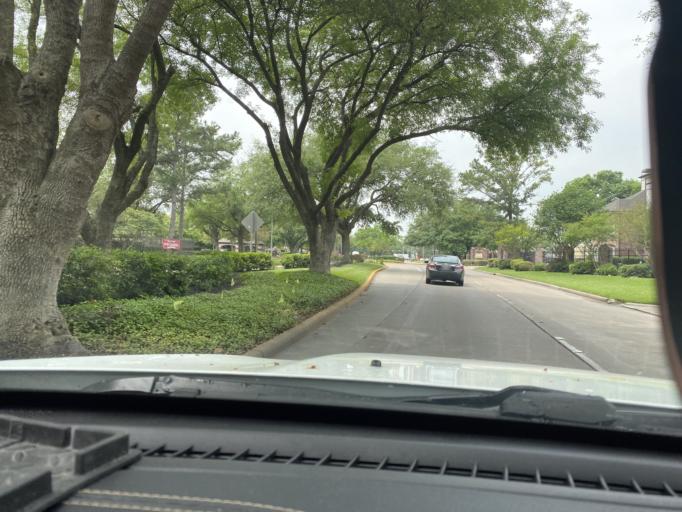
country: US
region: Texas
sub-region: Harris County
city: Jersey Village
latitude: 29.9100
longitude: -95.5814
